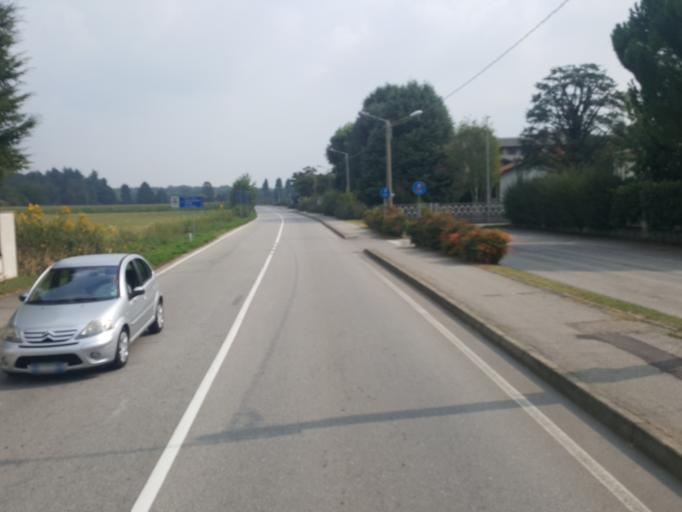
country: IT
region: Lombardy
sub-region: Provincia di Varese
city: Gorla Maggiore
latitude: 45.6634
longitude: 8.8977
